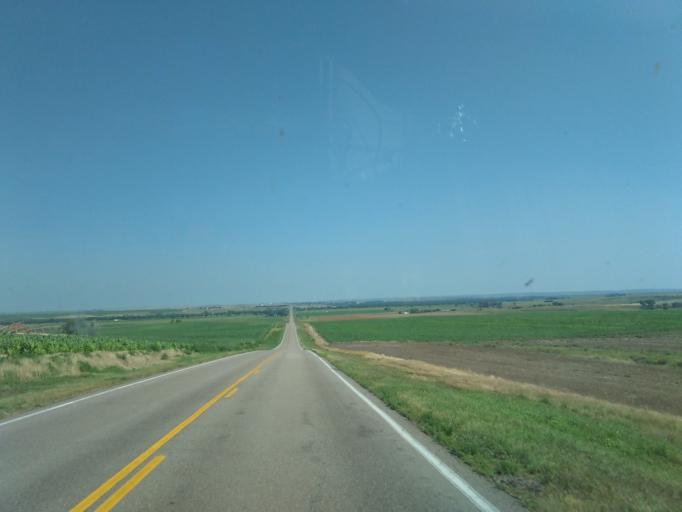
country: US
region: Nebraska
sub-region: Dundy County
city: Benkelman
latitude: 39.9791
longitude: -101.5418
